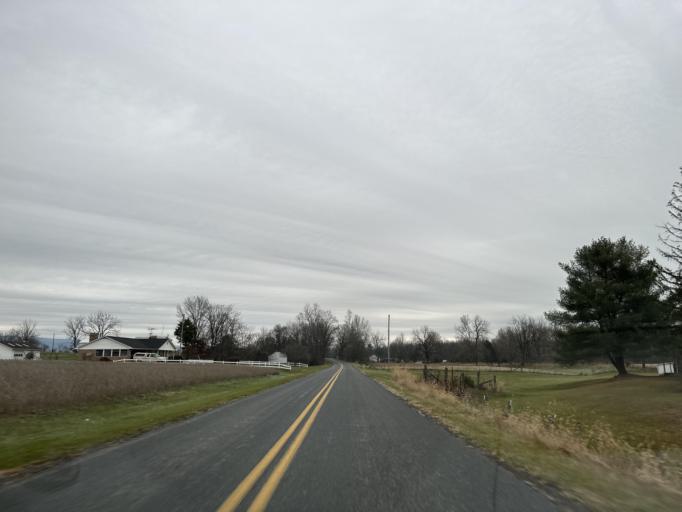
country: US
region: Virginia
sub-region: Rockingham County
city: Bridgewater
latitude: 38.3636
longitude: -79.0858
